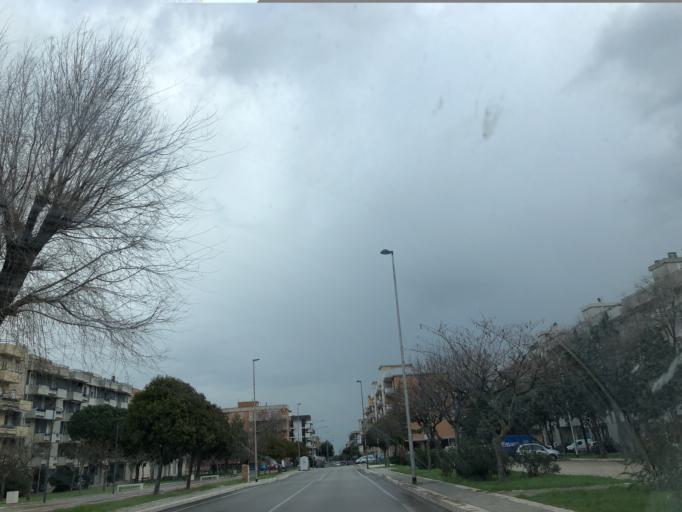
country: IT
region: Apulia
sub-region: Provincia di Foggia
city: Lucera
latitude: 41.5020
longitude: 15.3443
